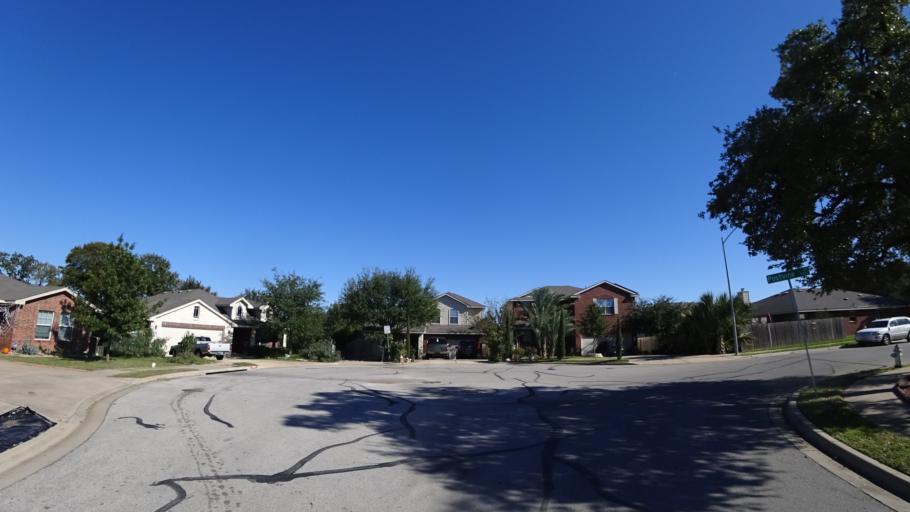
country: US
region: Texas
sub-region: Travis County
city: Hornsby Bend
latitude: 30.2753
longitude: -97.6313
